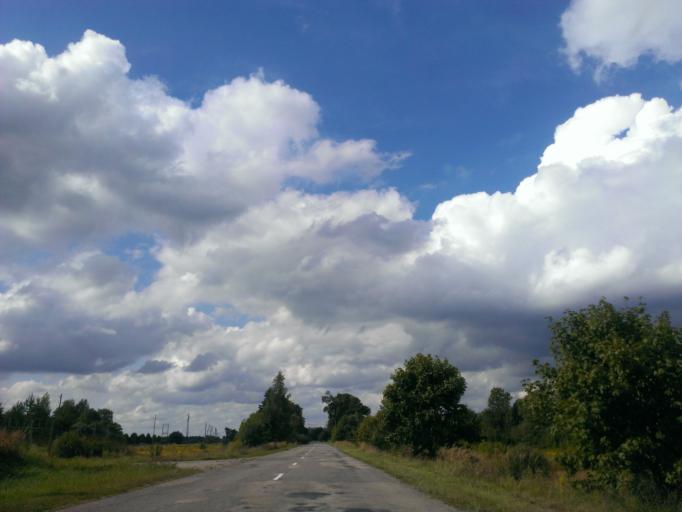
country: LV
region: Ropazu
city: Ropazi
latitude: 56.9629
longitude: 24.5322
